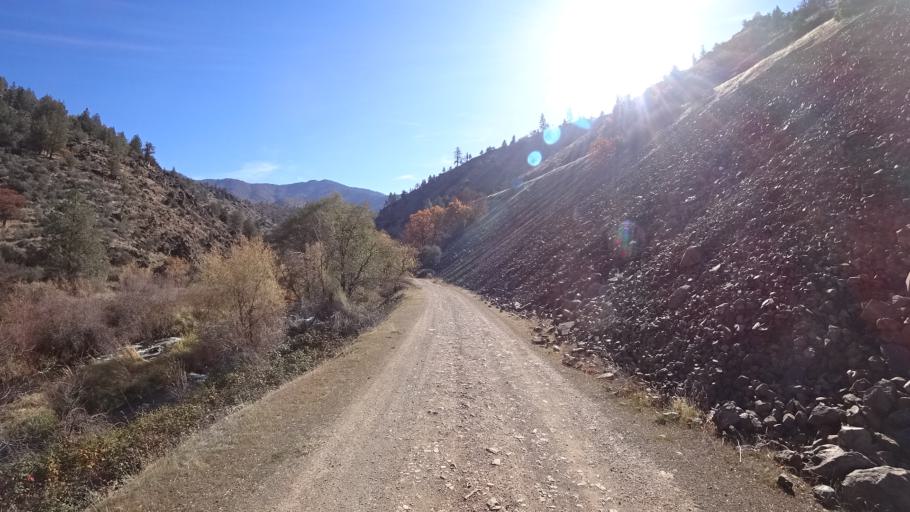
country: US
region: California
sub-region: Siskiyou County
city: Yreka
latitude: 41.8204
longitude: -122.5917
